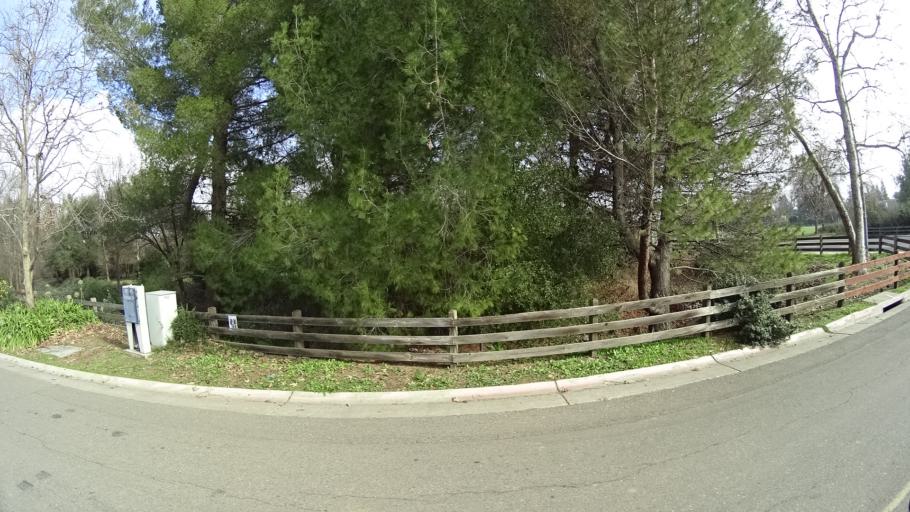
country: US
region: California
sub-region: Yolo County
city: Davis
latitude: 38.5415
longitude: -121.7212
